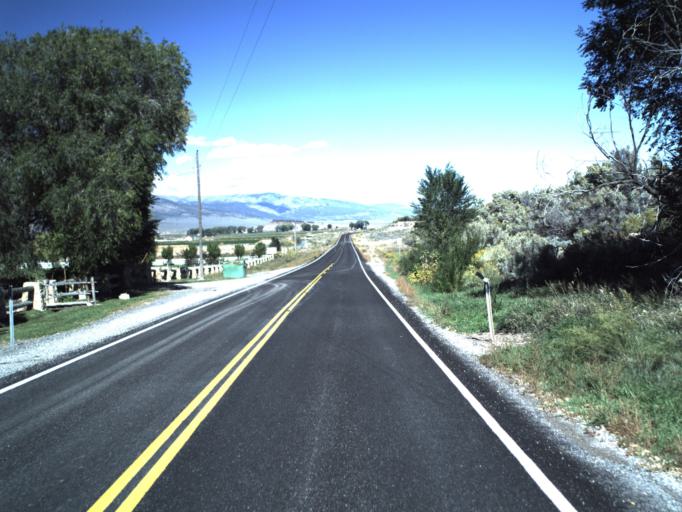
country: US
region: Utah
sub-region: Piute County
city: Junction
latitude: 38.1237
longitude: -112.0005
